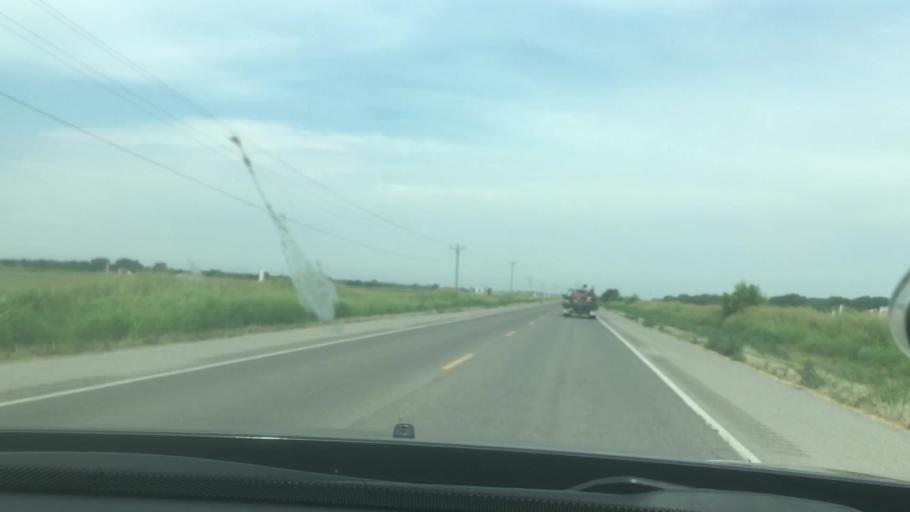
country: US
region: Oklahoma
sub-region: Garvin County
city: Lindsay
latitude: 34.8219
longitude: -97.5132
